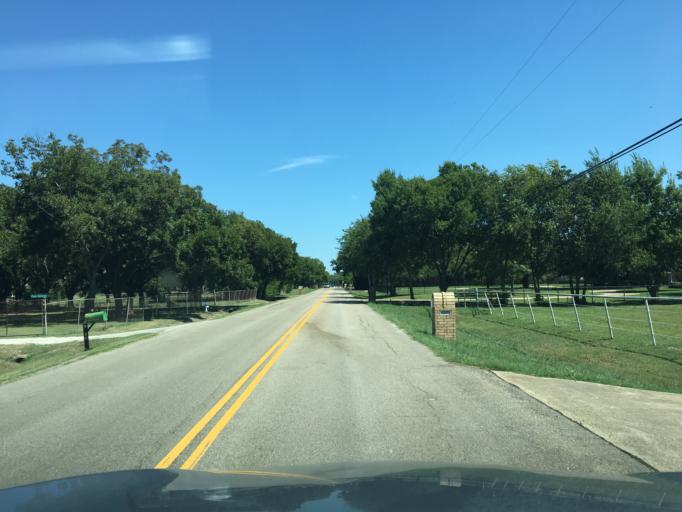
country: US
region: Texas
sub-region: Dallas County
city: Sachse
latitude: 32.9699
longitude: -96.6179
